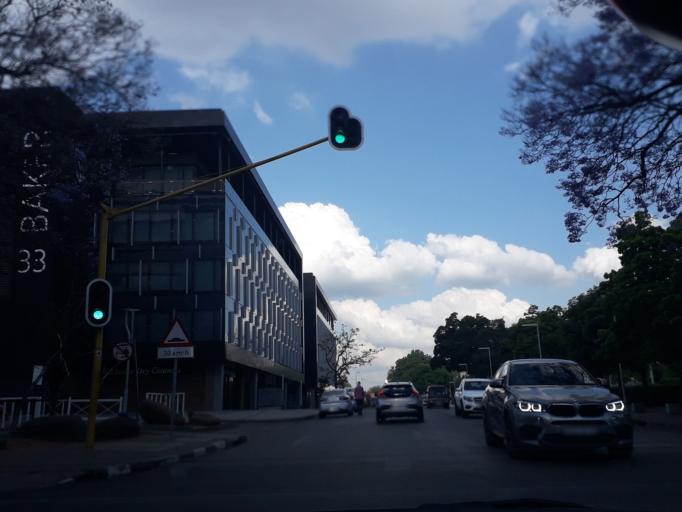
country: ZA
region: Gauteng
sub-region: City of Johannesburg Metropolitan Municipality
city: Johannesburg
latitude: -26.1477
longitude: 28.0426
